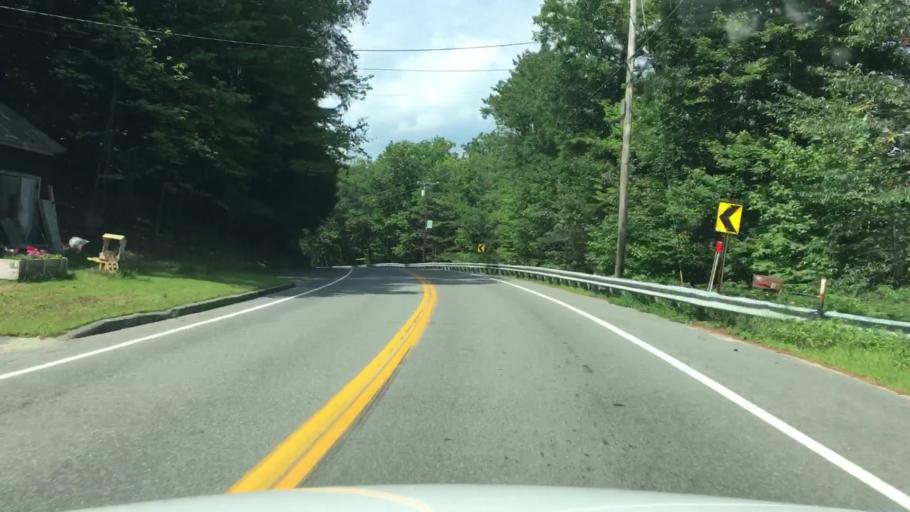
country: US
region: Maine
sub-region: Oxford County
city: Dixfield
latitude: 44.5293
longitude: -70.4663
